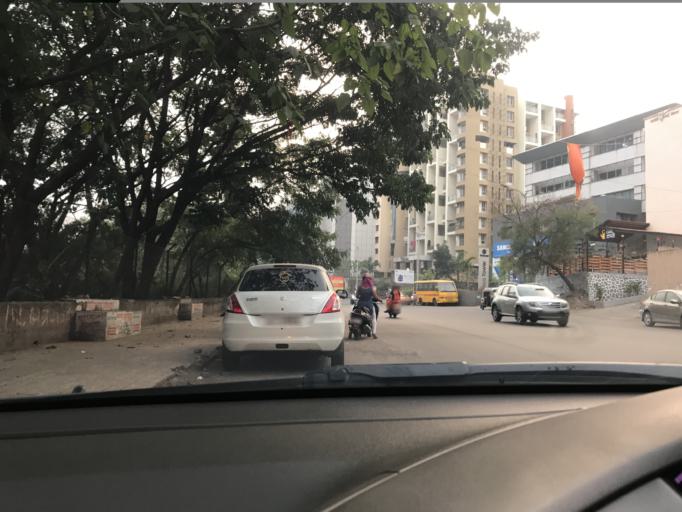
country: IN
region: Maharashtra
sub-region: Pune Division
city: Khadki
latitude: 18.5539
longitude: 73.7973
